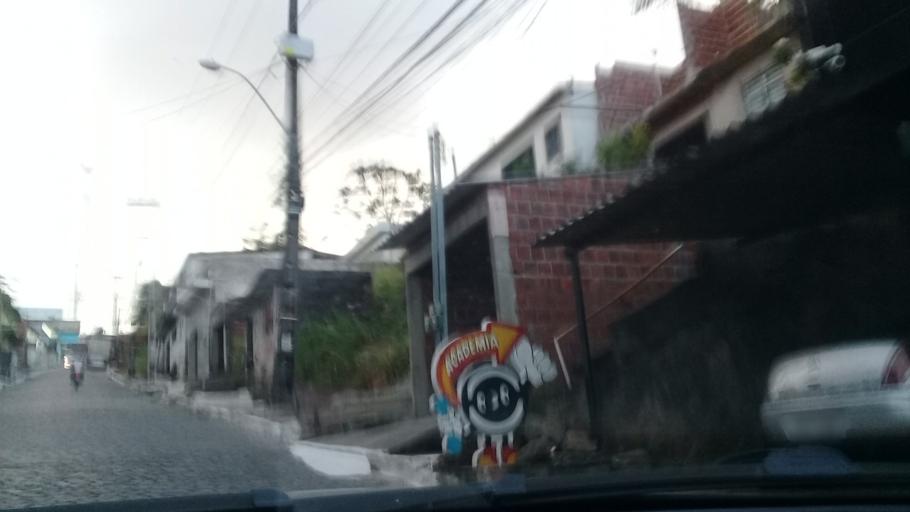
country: BR
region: Pernambuco
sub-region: Jaboatao Dos Guararapes
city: Jaboatao dos Guararapes
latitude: -8.1240
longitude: -34.9516
